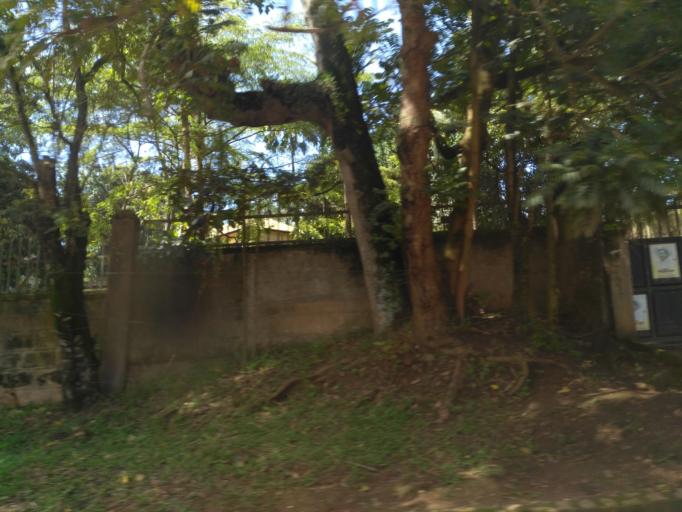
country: UG
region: Central Region
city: Kampala Central Division
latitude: 0.3294
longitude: 32.5801
